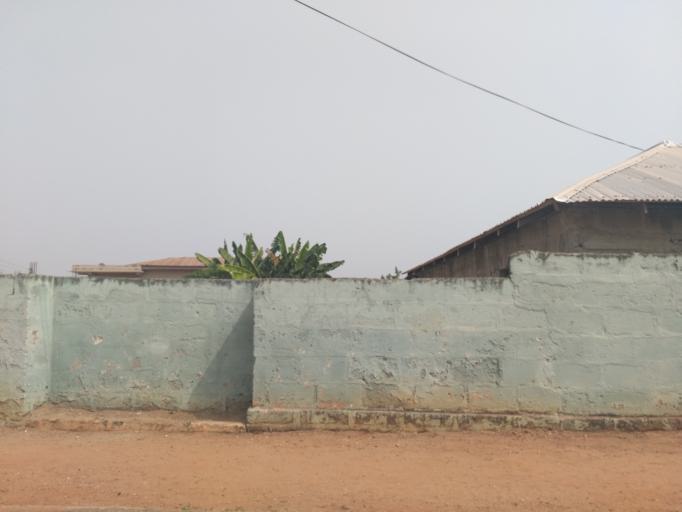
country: GH
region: Ashanti
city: Kumasi
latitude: 6.6828
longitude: -1.5978
